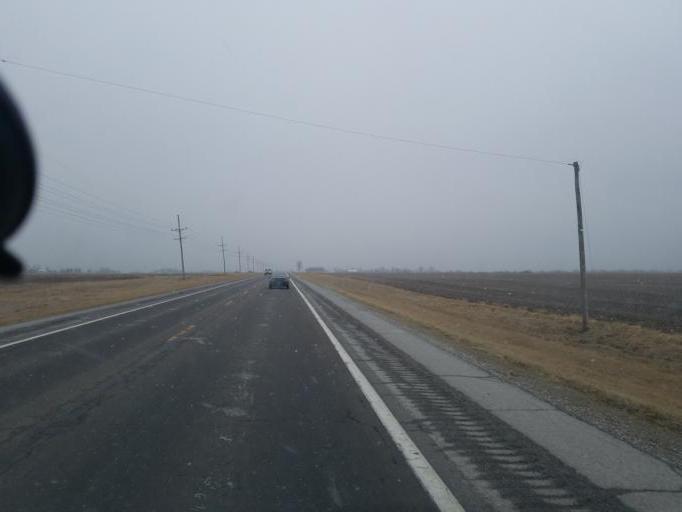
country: US
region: Missouri
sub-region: Schuyler County
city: Lancaster
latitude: 40.3843
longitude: -92.5589
